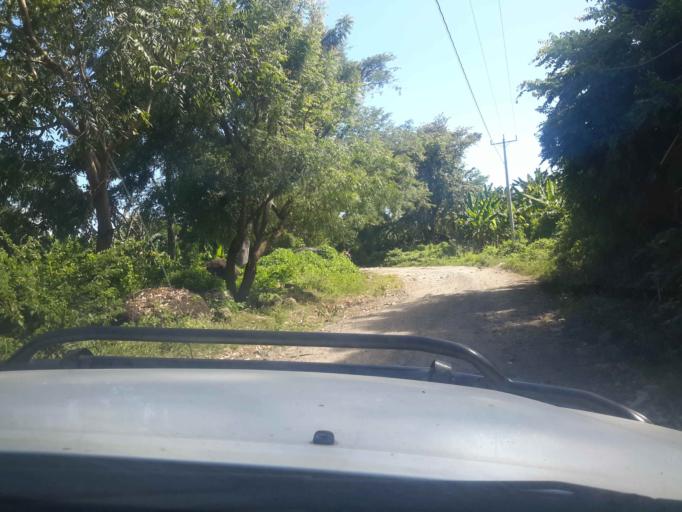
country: NI
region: Rivas
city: Altagracia
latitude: 11.4729
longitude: -85.4650
